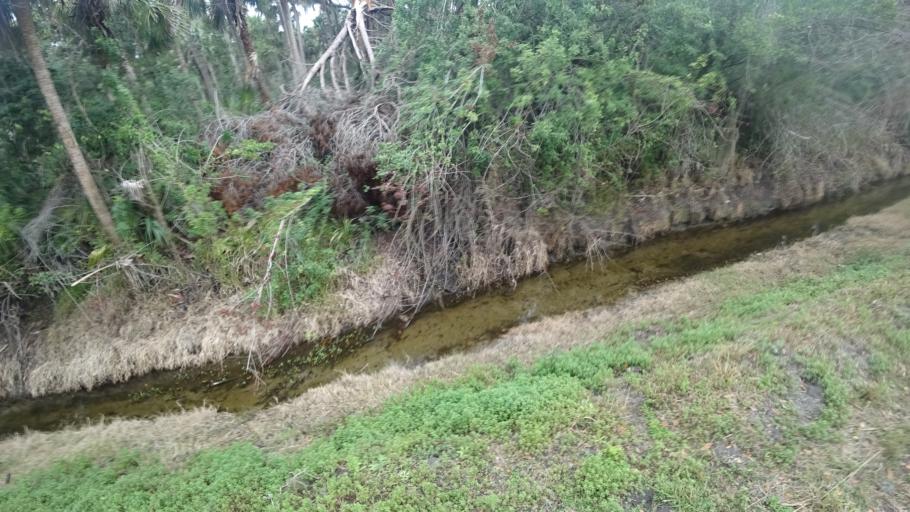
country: US
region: Florida
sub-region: Manatee County
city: Ellenton
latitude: 27.5793
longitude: -82.5006
